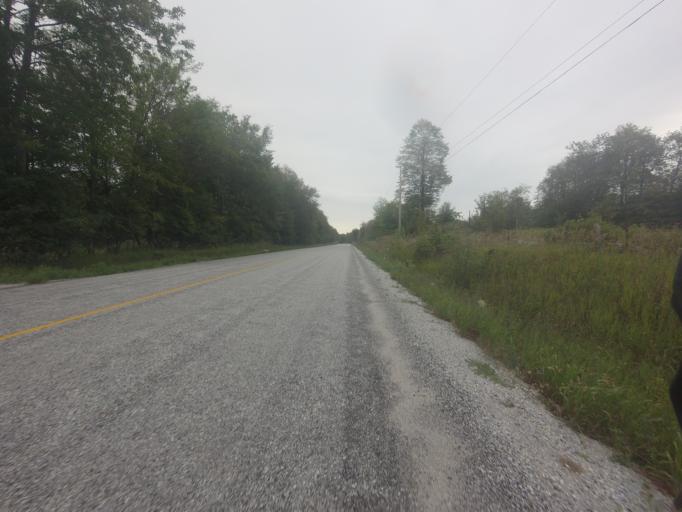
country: CA
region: Ontario
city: Perth
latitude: 44.8975
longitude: -76.4987
